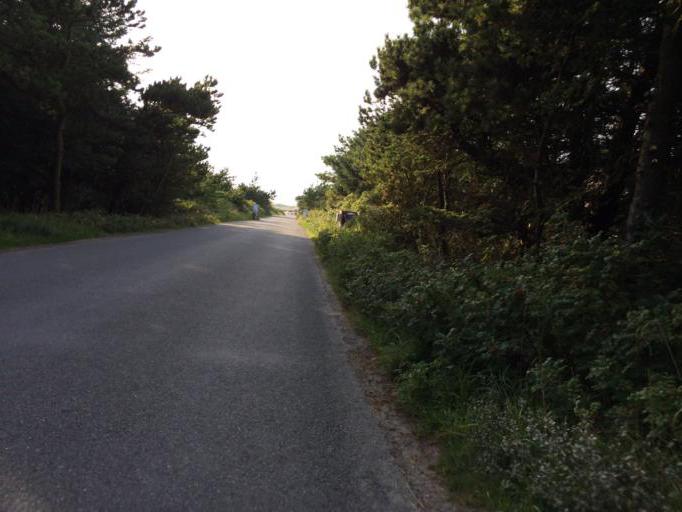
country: DK
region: Central Jutland
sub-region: Ringkobing-Skjern Kommune
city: Hvide Sande
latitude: 55.8678
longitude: 8.1728
